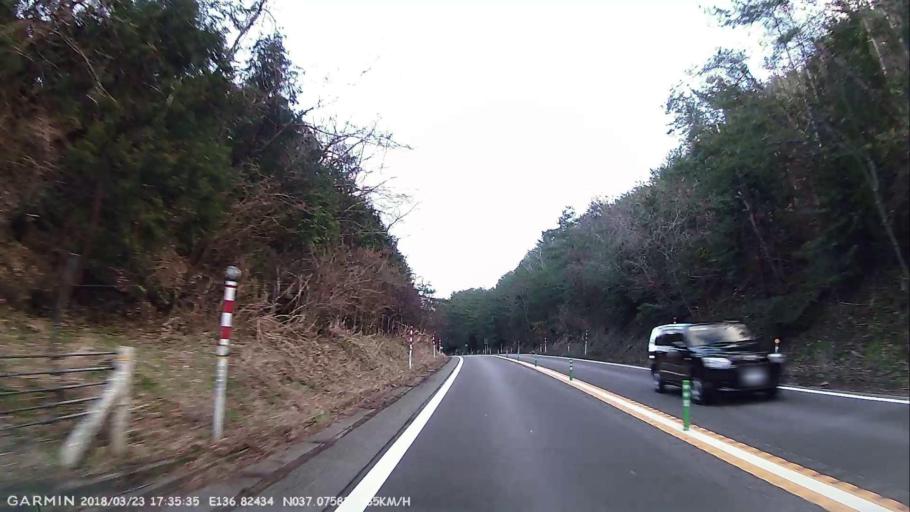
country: JP
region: Ishikawa
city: Nanao
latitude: 37.0760
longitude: 136.8243
